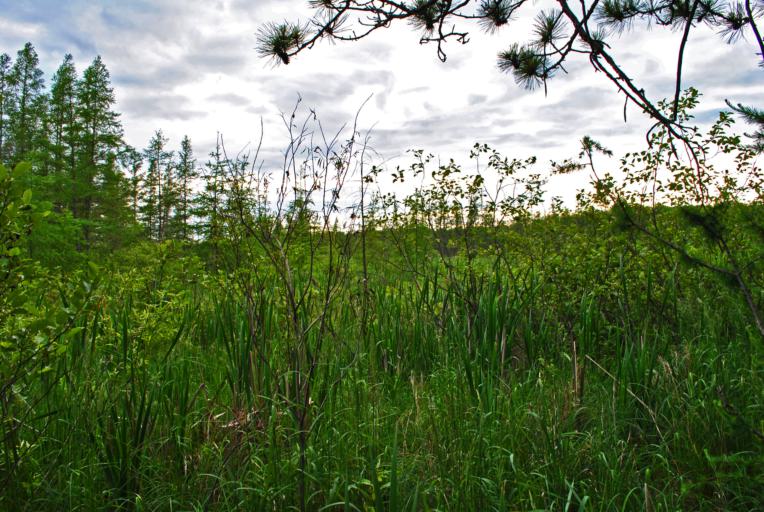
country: US
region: Wisconsin
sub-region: Vilas County
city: Eagle River
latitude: 45.7248
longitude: -89.1560
